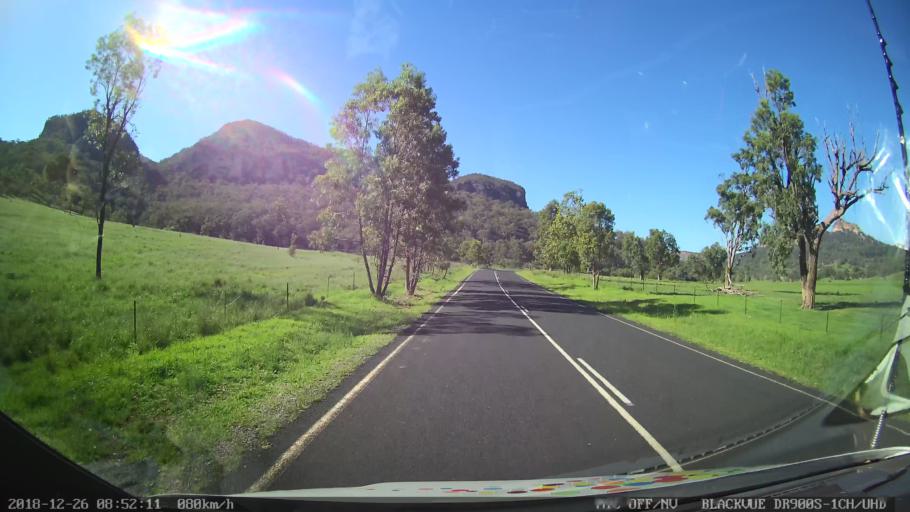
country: AU
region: New South Wales
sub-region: Mid-Western Regional
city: Kandos
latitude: -32.5940
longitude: 150.0872
